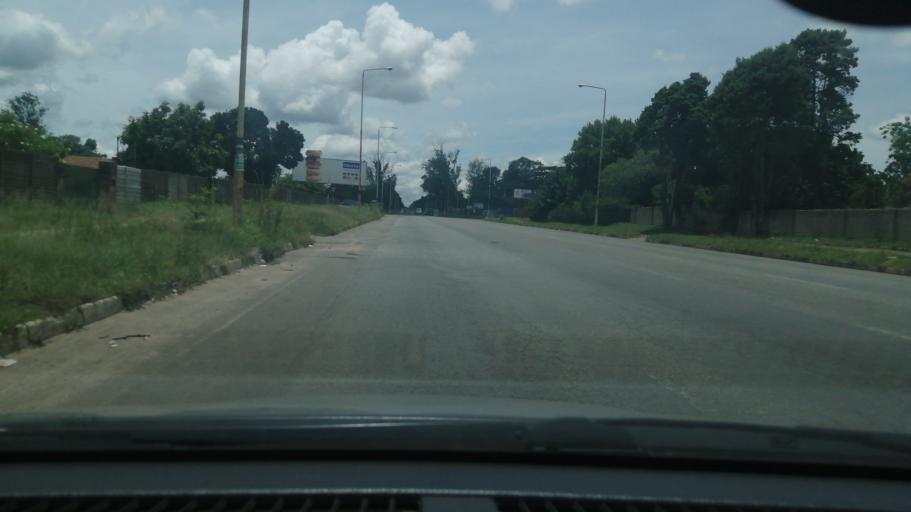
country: ZW
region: Harare
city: Harare
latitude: -17.8846
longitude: 31.0702
